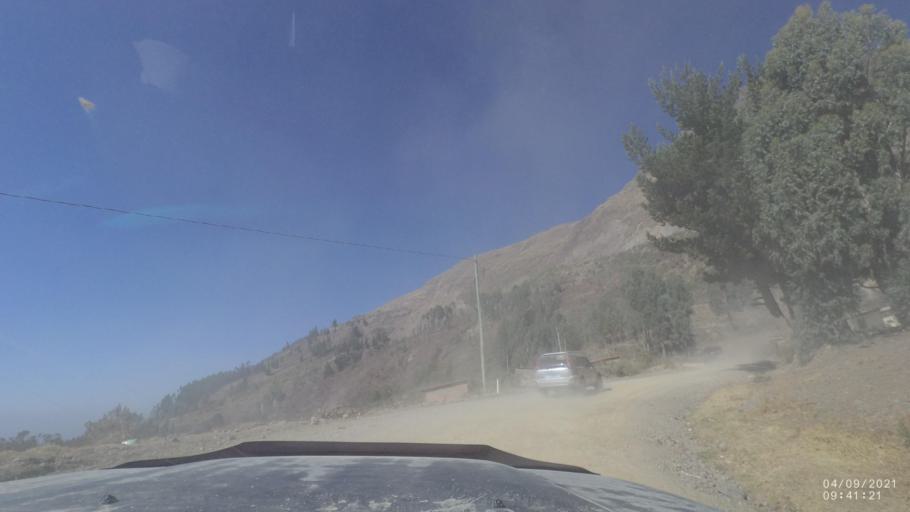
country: BO
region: Cochabamba
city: Sipe Sipe
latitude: -17.3403
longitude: -66.3880
